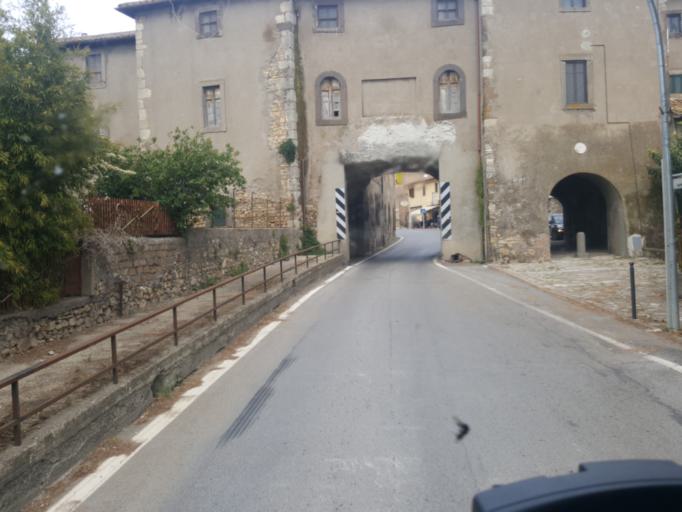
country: IT
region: Latium
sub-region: Provincia di Viterbo
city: Monte Romano
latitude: 42.2675
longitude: 11.8965
